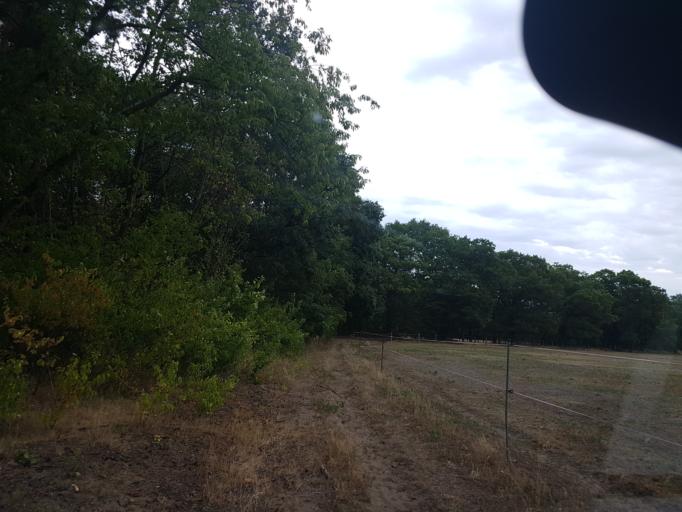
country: DE
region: Brandenburg
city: Schilda
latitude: 51.5717
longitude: 13.3449
